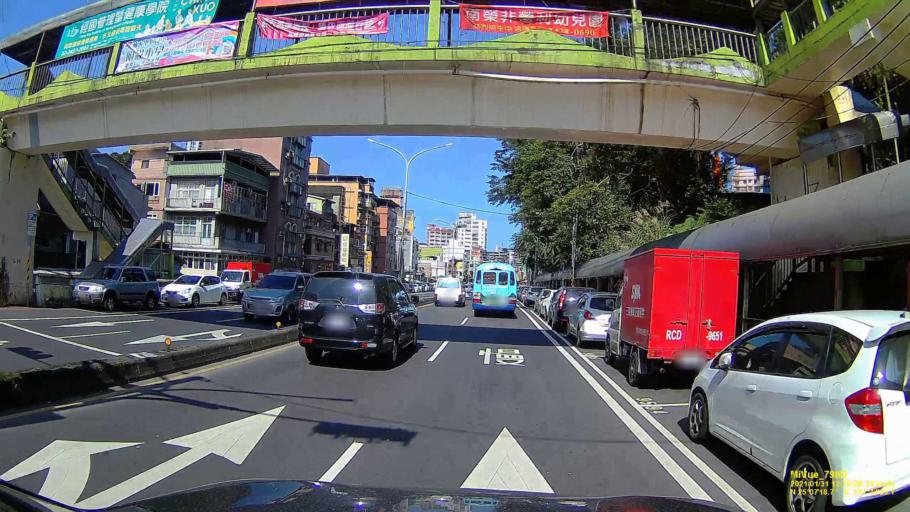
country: TW
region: Taiwan
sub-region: Keelung
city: Keelung
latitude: 25.1220
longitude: 121.7431
